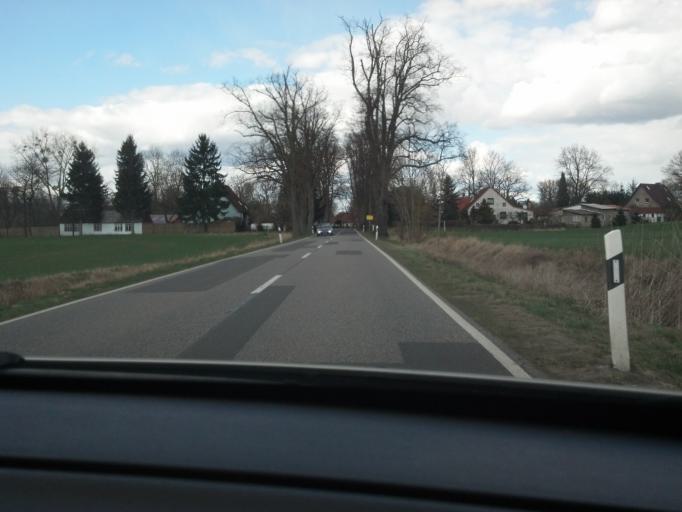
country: DE
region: Mecklenburg-Vorpommern
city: Loitz
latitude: 53.4189
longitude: 13.3577
